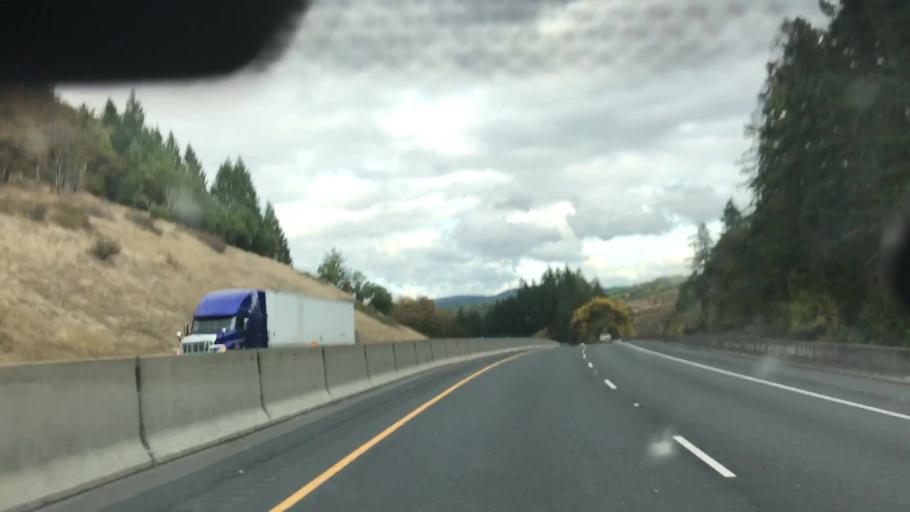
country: US
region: Oregon
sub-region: Douglas County
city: Yoncalla
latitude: 43.5268
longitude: -123.3080
